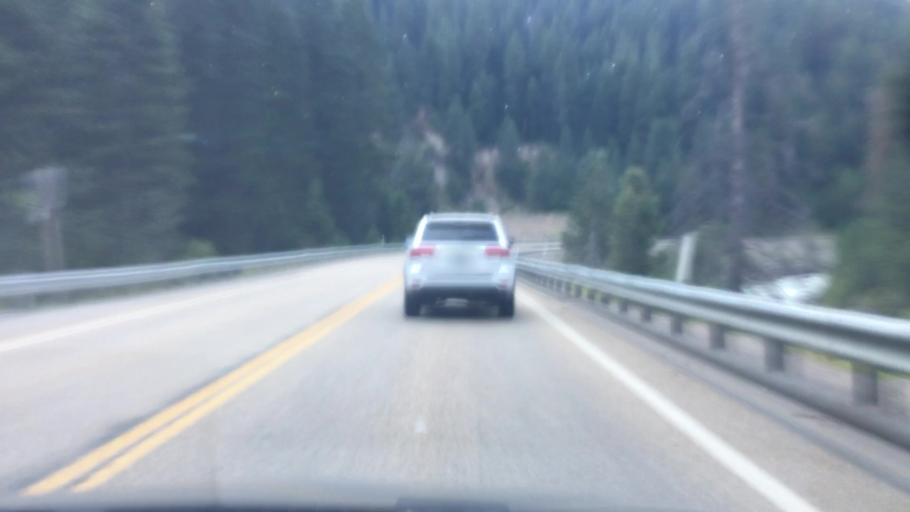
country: US
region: Idaho
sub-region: Valley County
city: Cascade
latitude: 44.1956
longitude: -116.1128
